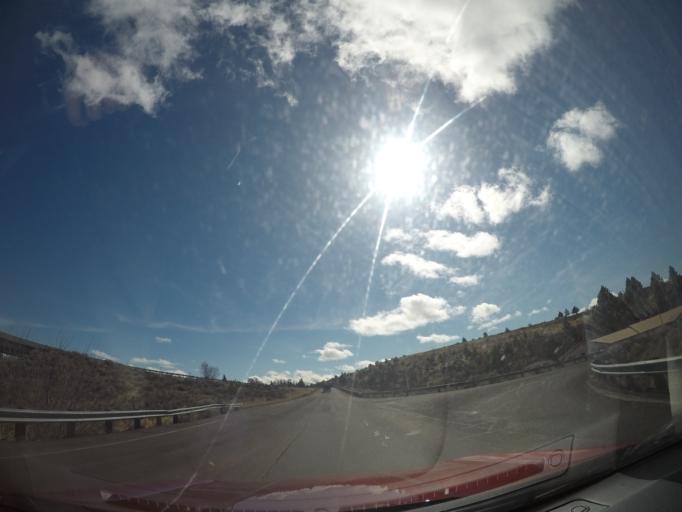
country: US
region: Oregon
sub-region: Klamath County
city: Klamath Falls
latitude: 42.2379
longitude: -121.7975
